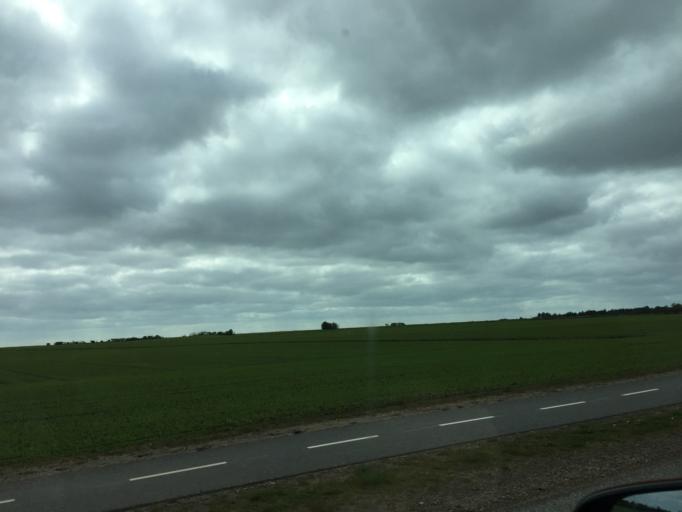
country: DK
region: Central Jutland
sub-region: Ringkobing-Skjern Kommune
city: Skjern
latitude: 55.9791
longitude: 8.3510
